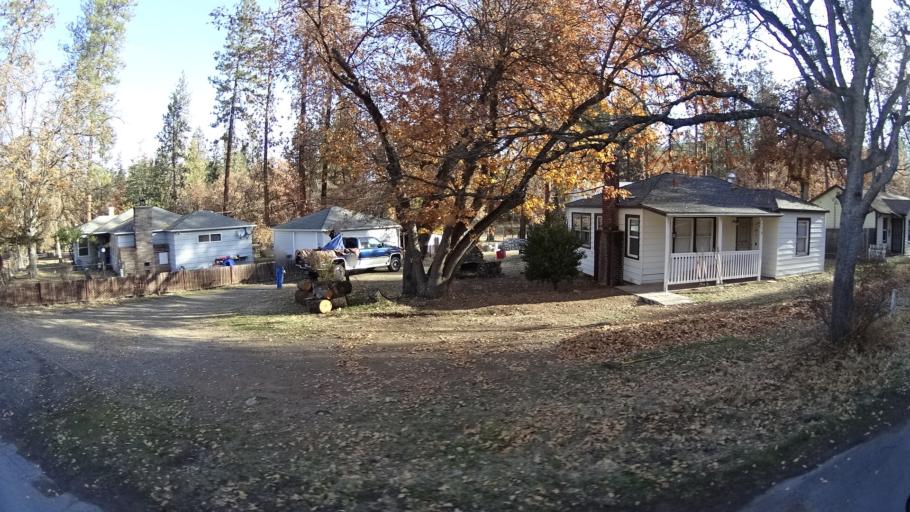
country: US
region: California
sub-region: Siskiyou County
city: Yreka
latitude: 41.6849
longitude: -122.6411
